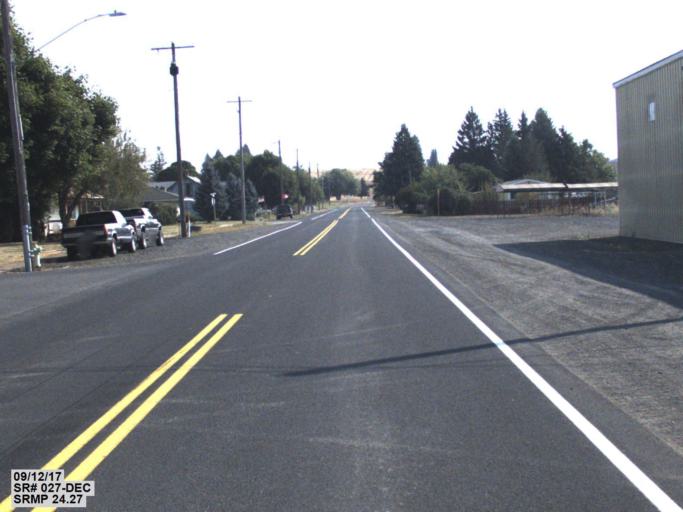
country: US
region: Washington
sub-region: Whitman County
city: Colfax
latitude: 47.0070
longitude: -117.1402
